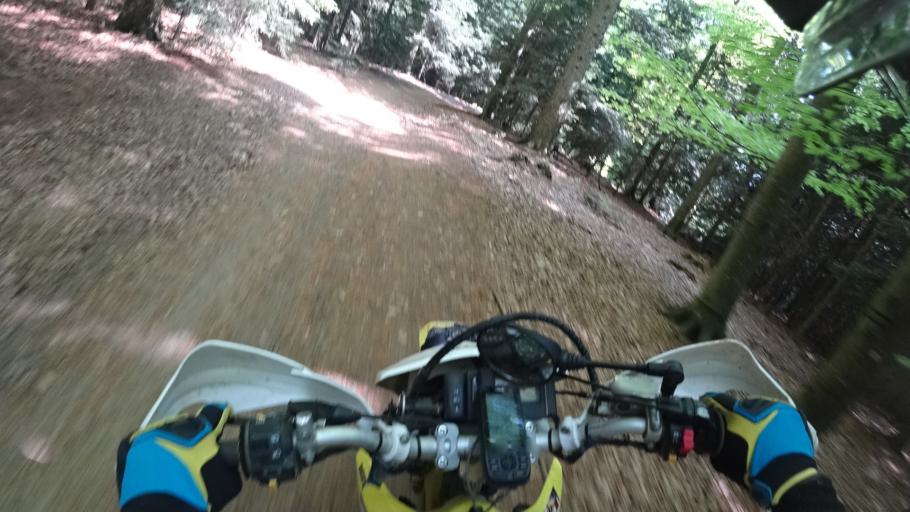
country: HR
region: Grad Zagreb
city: Kasina
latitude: 45.9140
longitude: 15.9455
